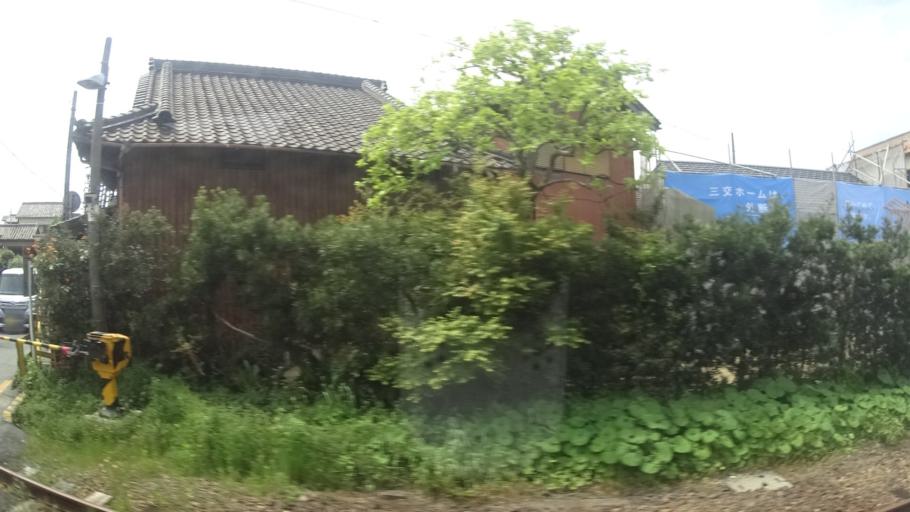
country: JP
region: Mie
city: Hisai-motomachi
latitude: 34.5900
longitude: 136.5214
